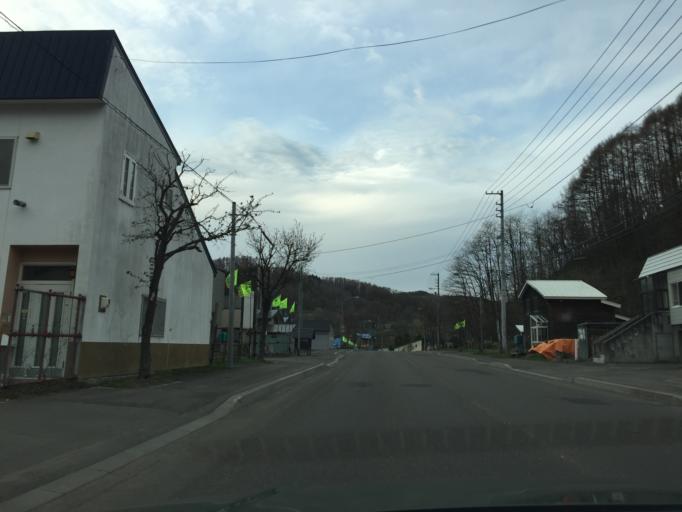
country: JP
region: Hokkaido
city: Utashinai
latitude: 43.5147
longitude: 142.0268
